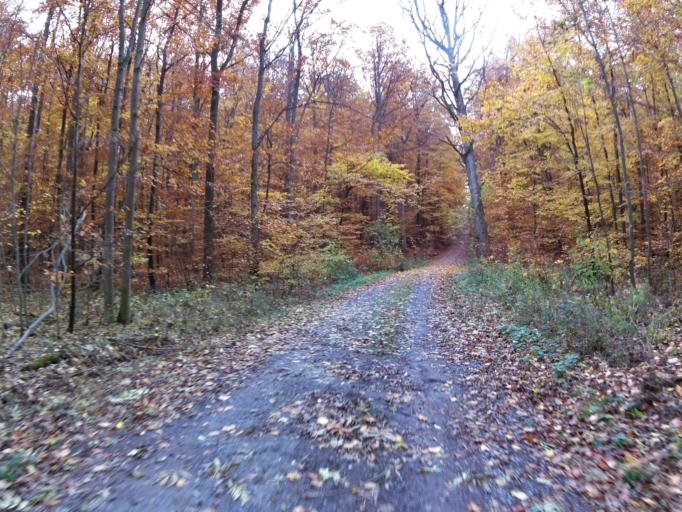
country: DE
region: Bavaria
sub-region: Regierungsbezirk Unterfranken
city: Kist
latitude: 49.7334
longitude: 9.8301
